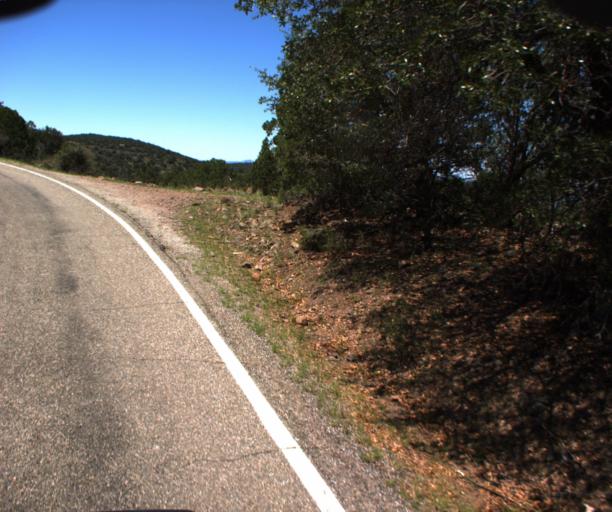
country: US
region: Arizona
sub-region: Greenlee County
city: Morenci
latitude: 33.2597
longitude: -109.3710
